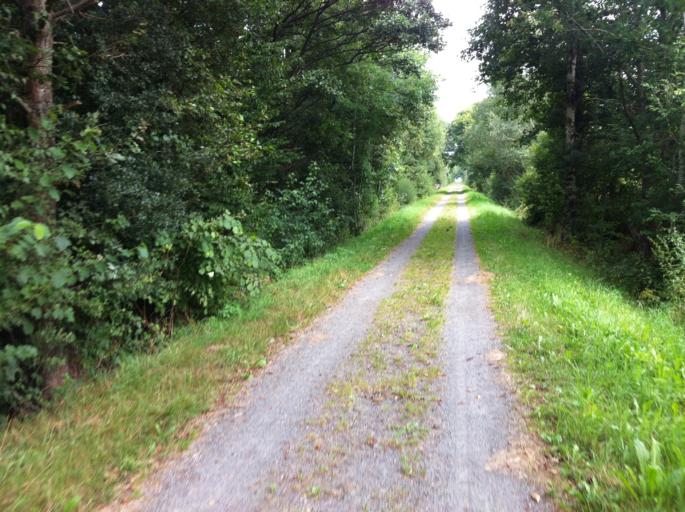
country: SE
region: Skane
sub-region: Kristianstads Kommun
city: Onnestad
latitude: 55.9405
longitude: 13.9212
